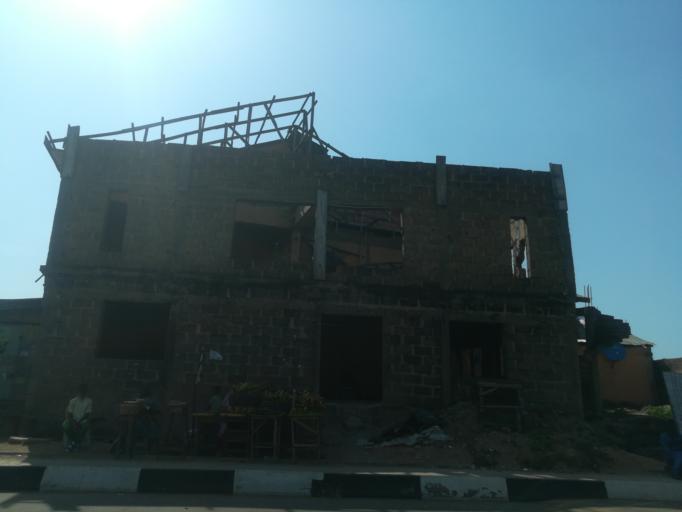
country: NG
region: Ogun
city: Abeokuta
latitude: 7.1411
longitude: 3.3307
